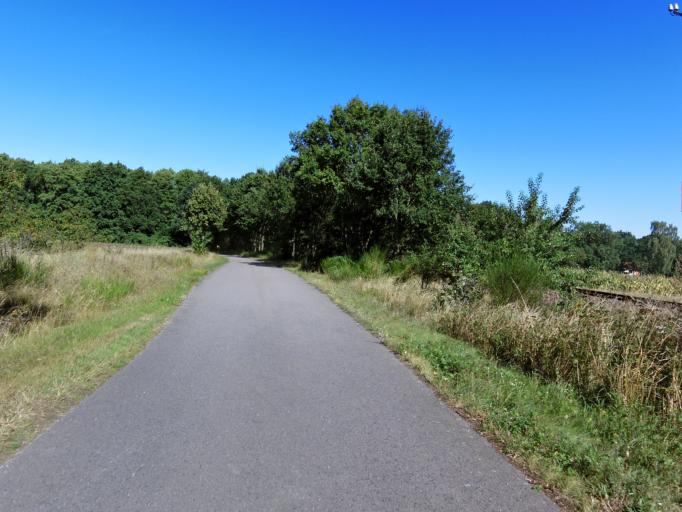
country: DE
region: Saxony-Anhalt
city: Pretzsch
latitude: 51.6732
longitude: 12.8263
